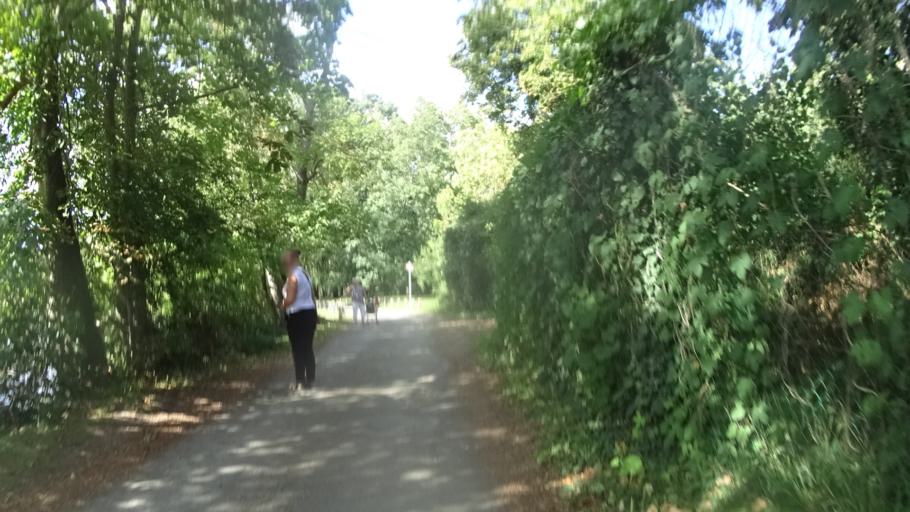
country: FR
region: Ile-de-France
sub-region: Departement de l'Essonne
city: Vert-le-Petit
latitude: 48.5458
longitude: 2.3720
